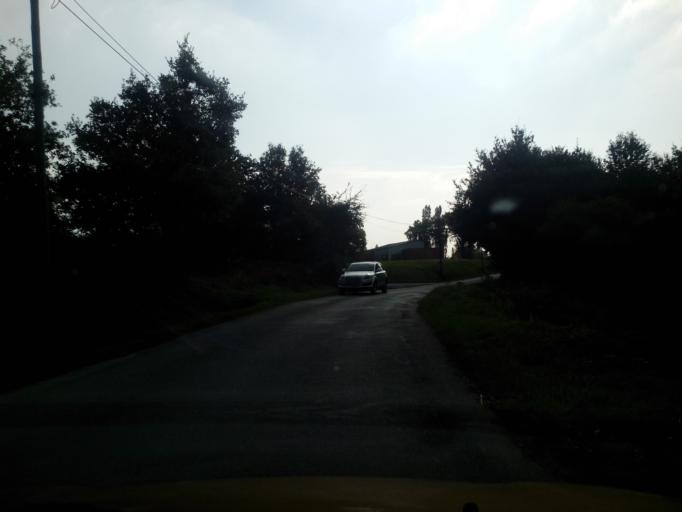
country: FR
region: Brittany
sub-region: Departement du Morbihan
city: Molac
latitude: 47.7340
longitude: -2.4384
